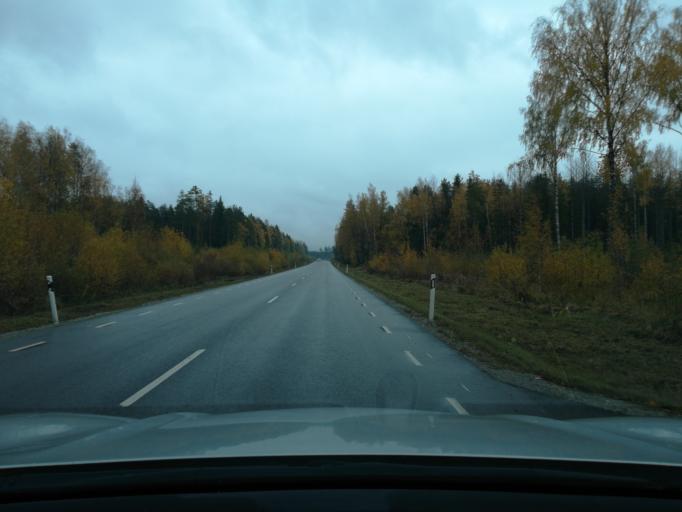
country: EE
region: Ida-Virumaa
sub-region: Johvi vald
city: Johvi
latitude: 59.3063
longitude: 27.4614
